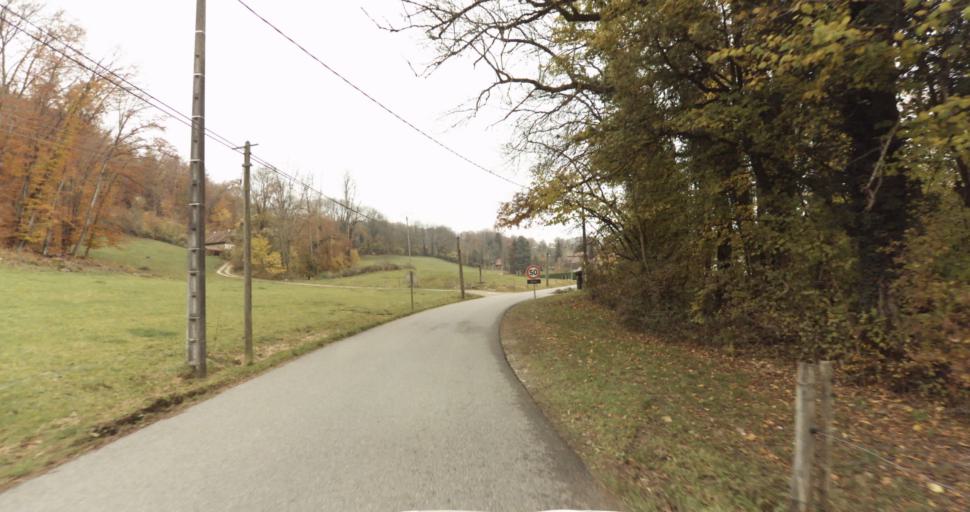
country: FR
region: Rhone-Alpes
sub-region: Departement de la Haute-Savoie
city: Cusy
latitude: 45.7542
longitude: 6.0174
